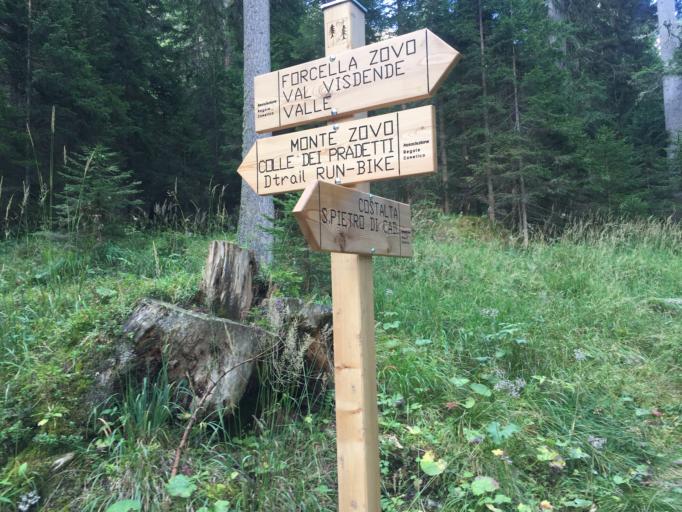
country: IT
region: Veneto
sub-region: Provincia di Belluno
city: San Pietro di Cadore
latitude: 46.6084
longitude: 12.5718
